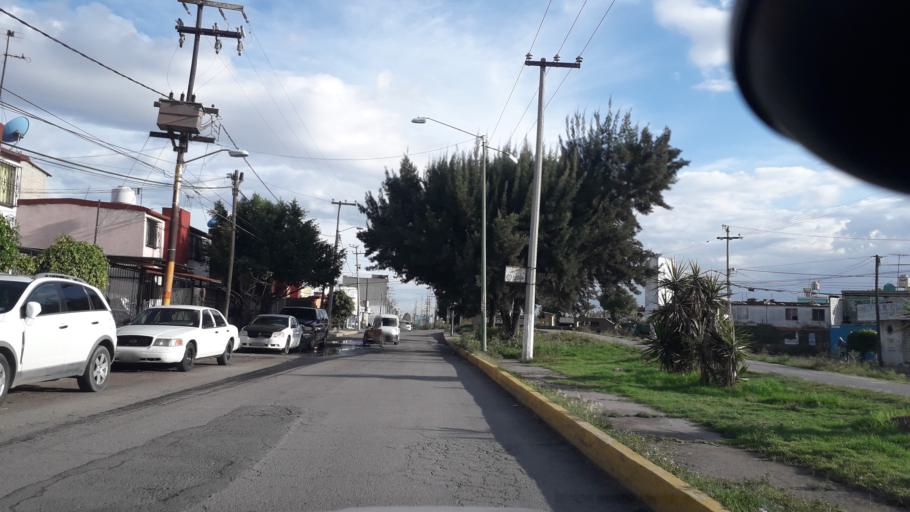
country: MX
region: Mexico
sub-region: Jaltenco
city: Alborada Jaltenco
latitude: 19.6665
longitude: -99.0748
